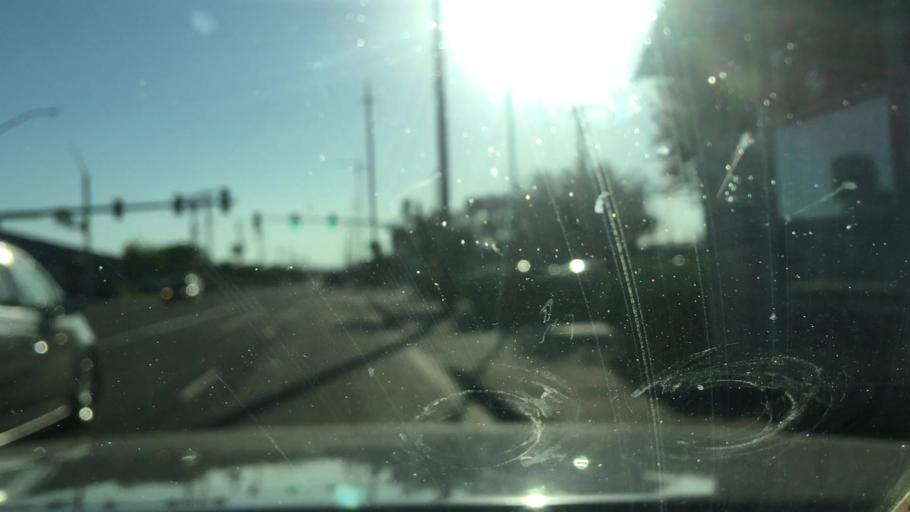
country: US
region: Oregon
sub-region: Lane County
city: Eugene
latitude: 44.0479
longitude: -123.1291
